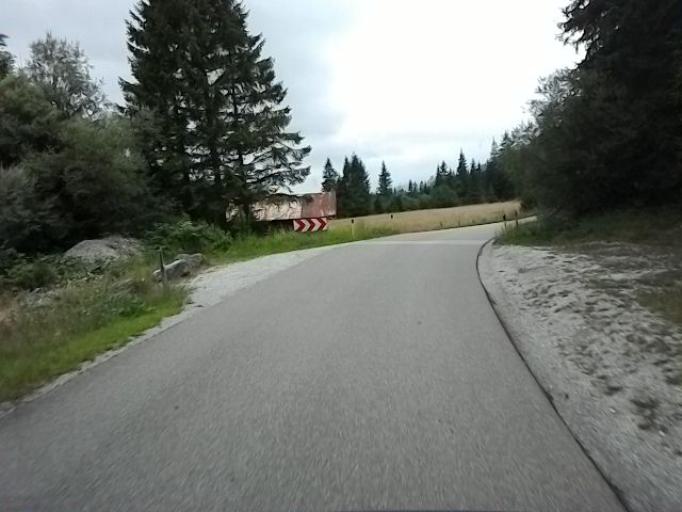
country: DE
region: Bavaria
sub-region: Upper Bavaria
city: Wallgau
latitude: 47.5418
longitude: 11.3540
